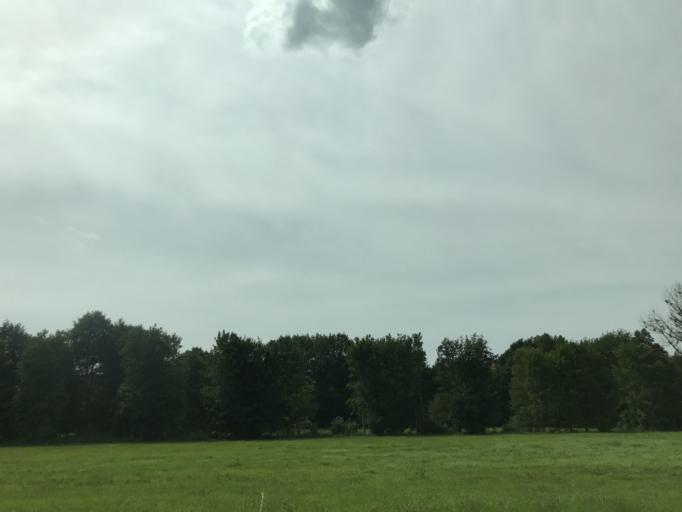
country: DE
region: Thuringia
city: Weissenborn-Luderode
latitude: 51.5465
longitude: 10.3869
